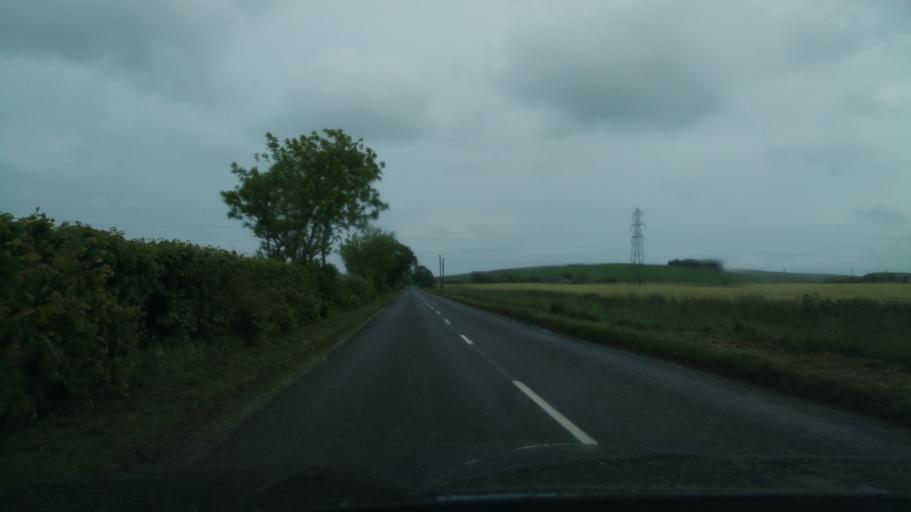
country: GB
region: Scotland
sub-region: Aberdeenshire
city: Portsoy
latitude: 57.6677
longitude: -2.6915
